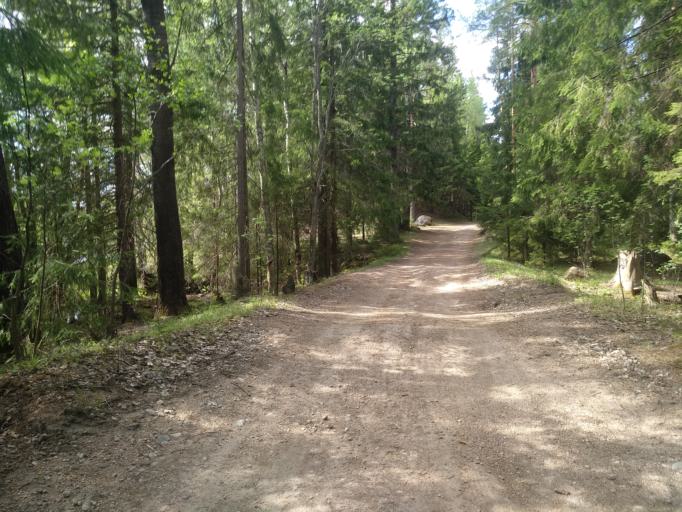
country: RU
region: Leningrad
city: Veshchevo
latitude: 60.7548
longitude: 29.1168
